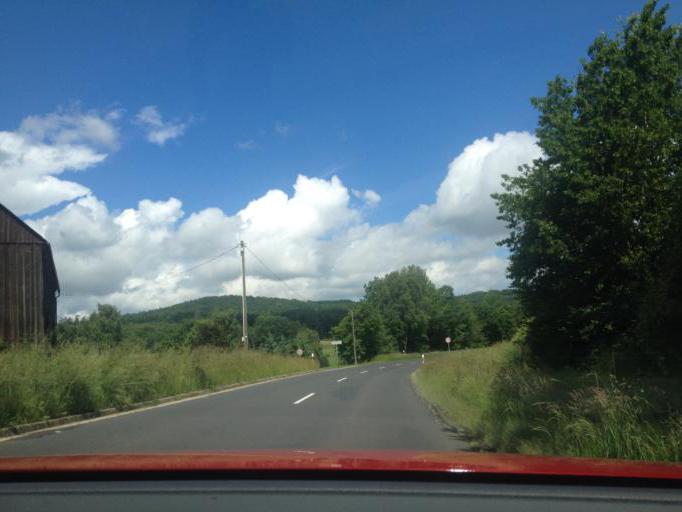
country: DE
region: Bavaria
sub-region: Upper Palatinate
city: Pechbrunn
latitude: 49.9786
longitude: 12.1748
